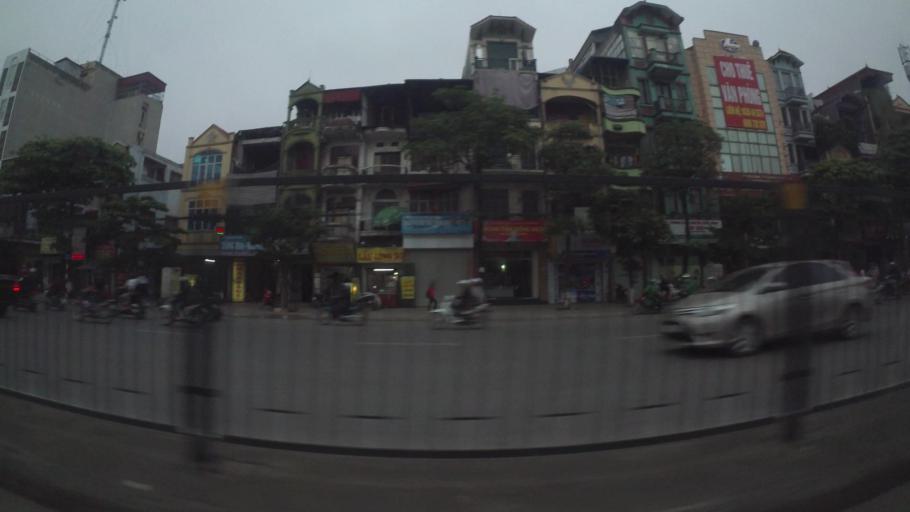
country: VN
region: Ha Noi
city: Van Dien
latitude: 20.9779
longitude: 105.8410
